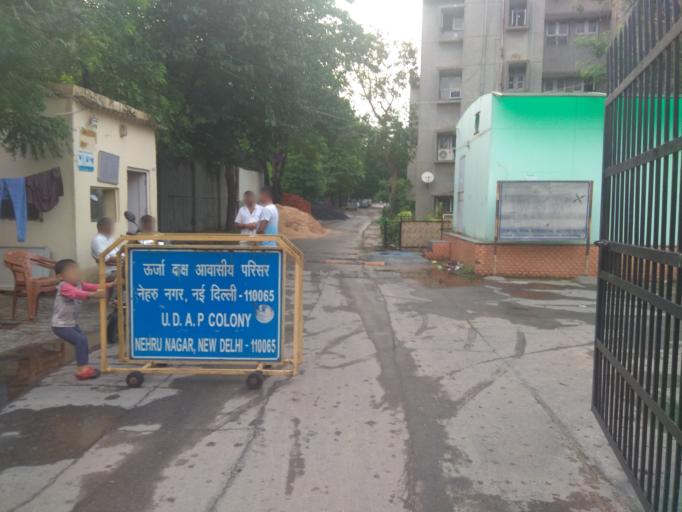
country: IN
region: NCT
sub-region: New Delhi
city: New Delhi
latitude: 28.5700
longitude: 77.2502
